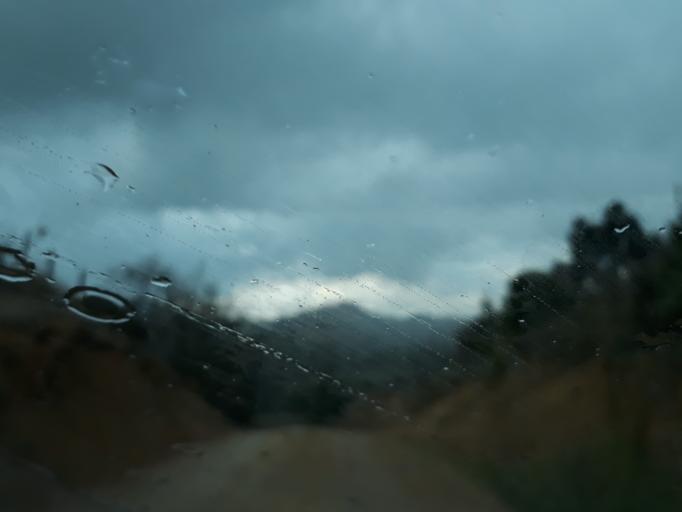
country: CO
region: Cundinamarca
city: Villapinzon
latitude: 5.2935
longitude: -73.6192
